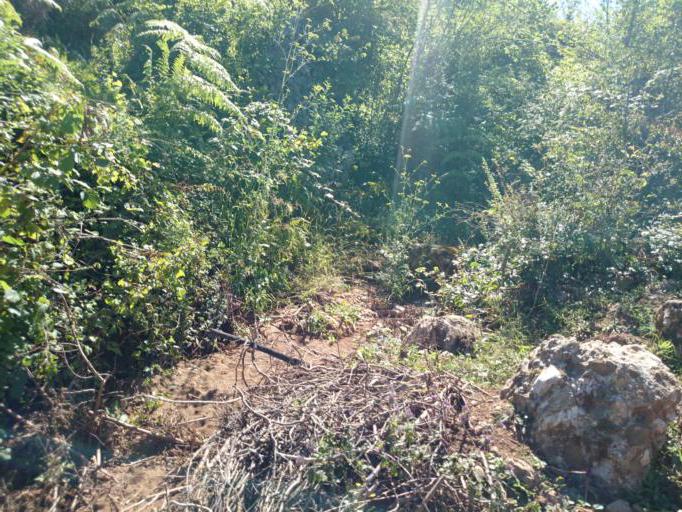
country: AL
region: Elbasan
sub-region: Rrethi i Gramshit
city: Porocan
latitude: 40.9234
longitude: 20.2873
